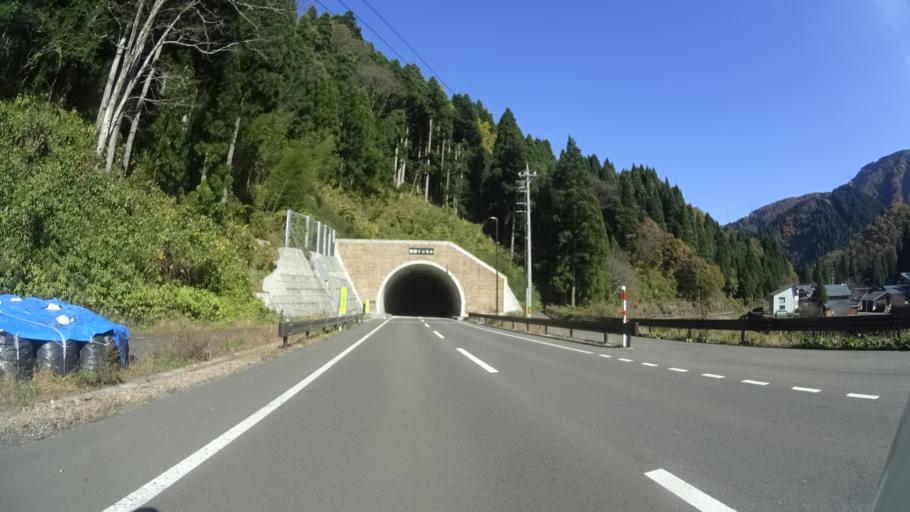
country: JP
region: Fukui
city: Ono
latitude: 35.9293
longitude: 136.3529
